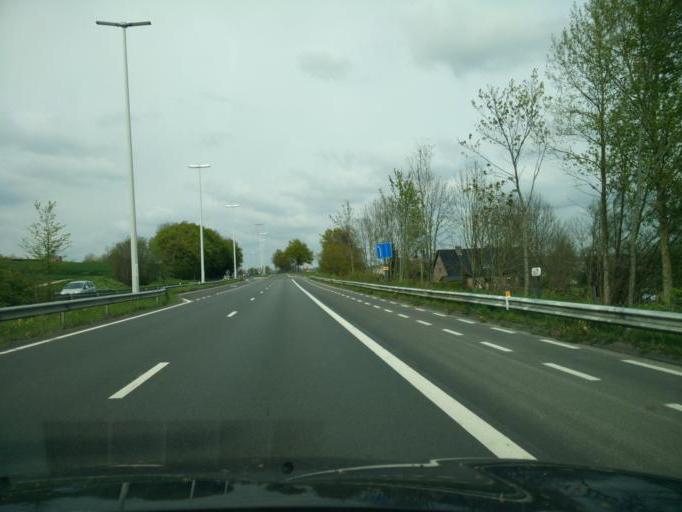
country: BE
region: Flanders
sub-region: Provincie Oost-Vlaanderen
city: Oudenaarde
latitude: 50.8093
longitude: 3.6002
